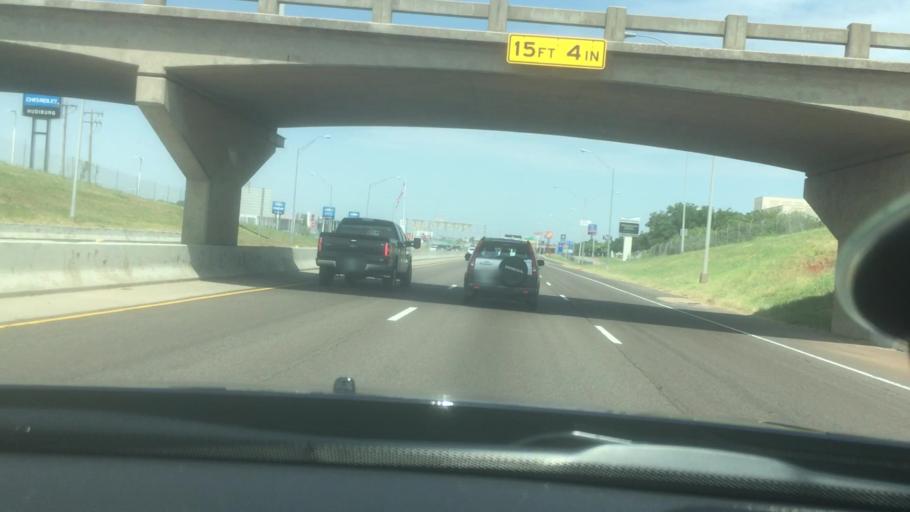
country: US
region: Oklahoma
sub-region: Oklahoma County
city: Midwest City
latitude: 35.4401
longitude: -97.4159
